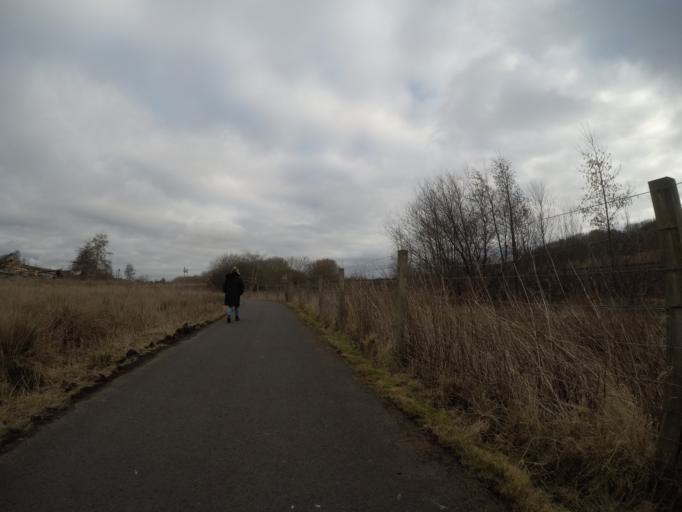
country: GB
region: Scotland
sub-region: North Ayrshire
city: Dreghorn
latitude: 55.5715
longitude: -4.6363
